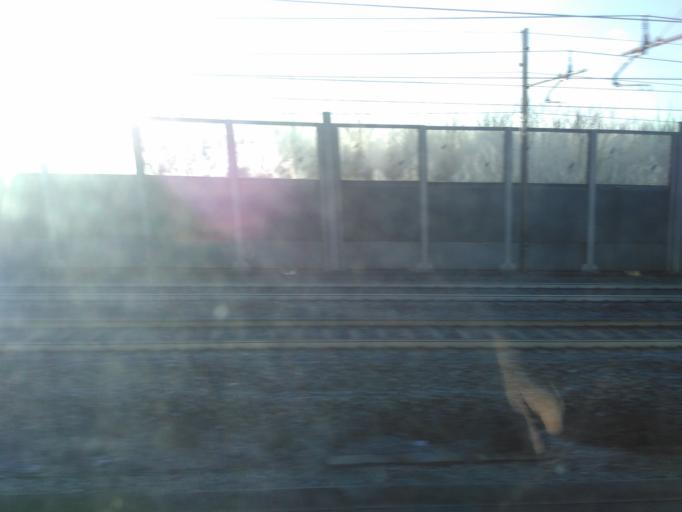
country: IT
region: Veneto
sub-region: Provincia di Padova
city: Vigonza
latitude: 45.4357
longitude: 11.9810
